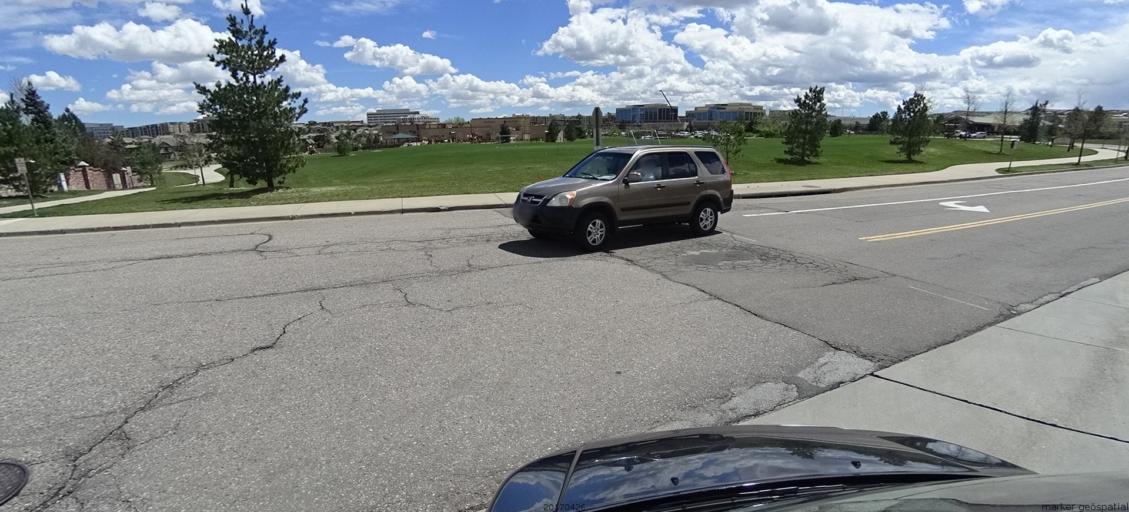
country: US
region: Colorado
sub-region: Adams County
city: Lone Tree
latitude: 39.5390
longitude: -104.8828
